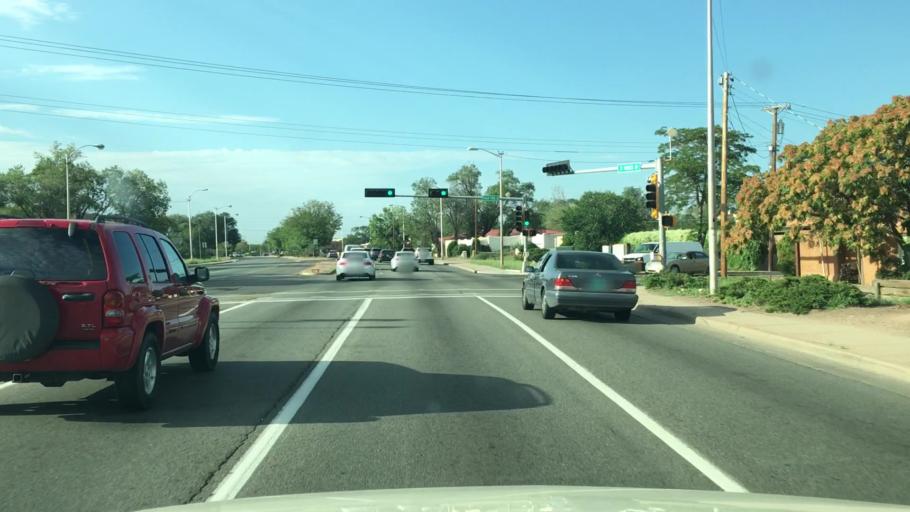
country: US
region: New Mexico
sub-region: Santa Fe County
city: Santa Fe
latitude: 35.6846
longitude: -105.9550
